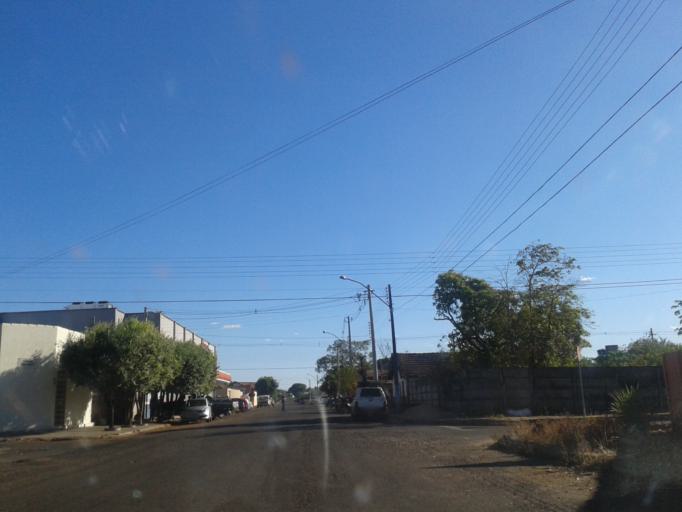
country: BR
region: Goias
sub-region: Sao Miguel Do Araguaia
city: Sao Miguel do Araguaia
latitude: -13.2778
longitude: -50.1596
